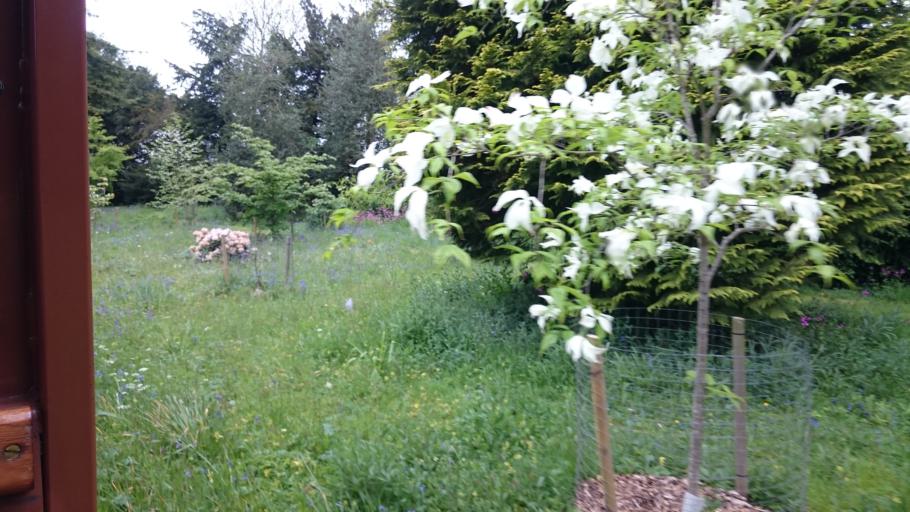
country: GB
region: England
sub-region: Oxfordshire
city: Burford
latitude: 51.7745
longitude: -1.6569
